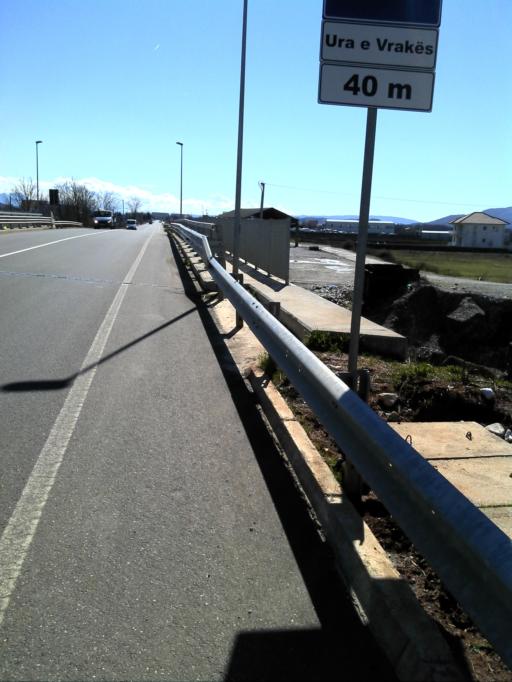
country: AL
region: Shkoder
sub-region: Rrethi i Malesia e Madhe
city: Grude-Fushe
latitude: 42.1226
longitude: 19.4948
